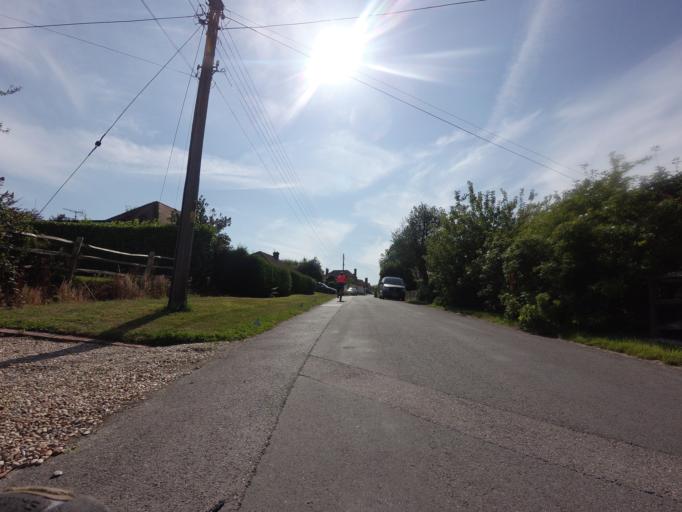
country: GB
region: England
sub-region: East Sussex
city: Rye
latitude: 50.9823
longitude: 0.7325
